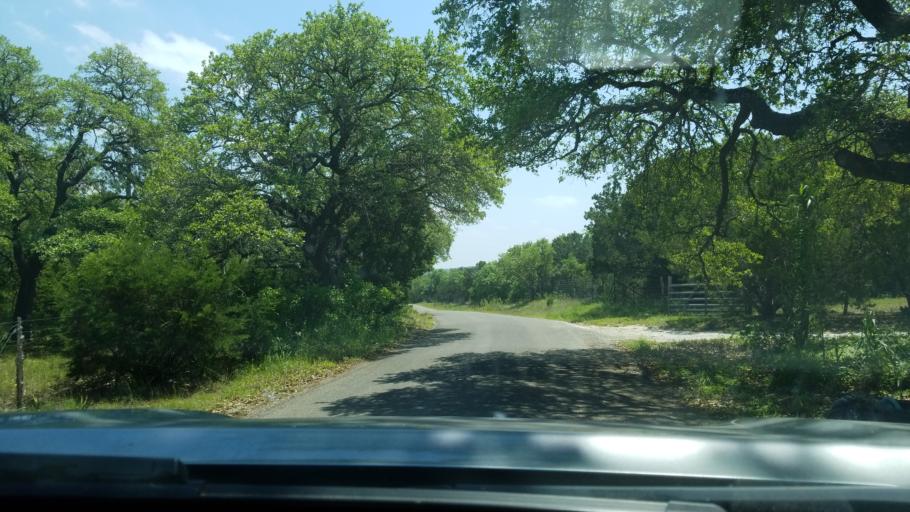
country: US
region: Texas
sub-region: Blanco County
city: Blanco
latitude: 30.0806
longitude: -98.4009
